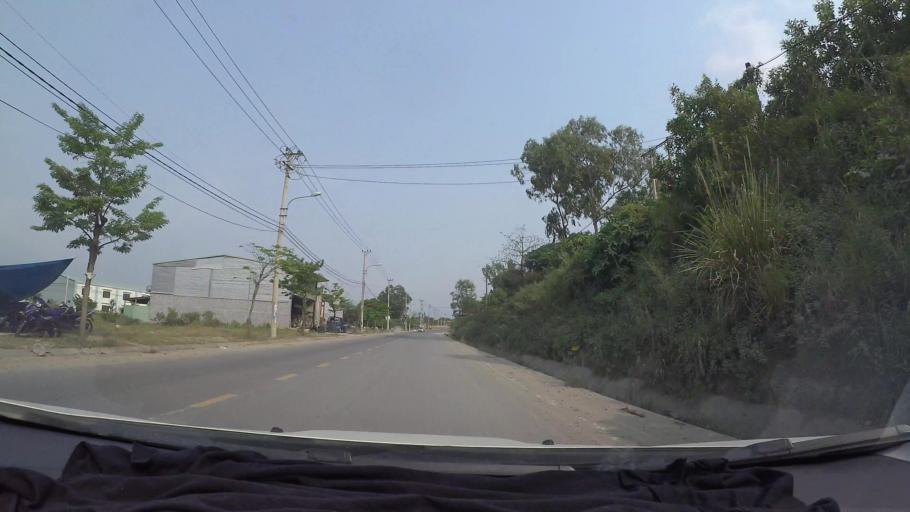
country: VN
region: Da Nang
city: Lien Chieu
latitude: 16.0403
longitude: 108.1692
